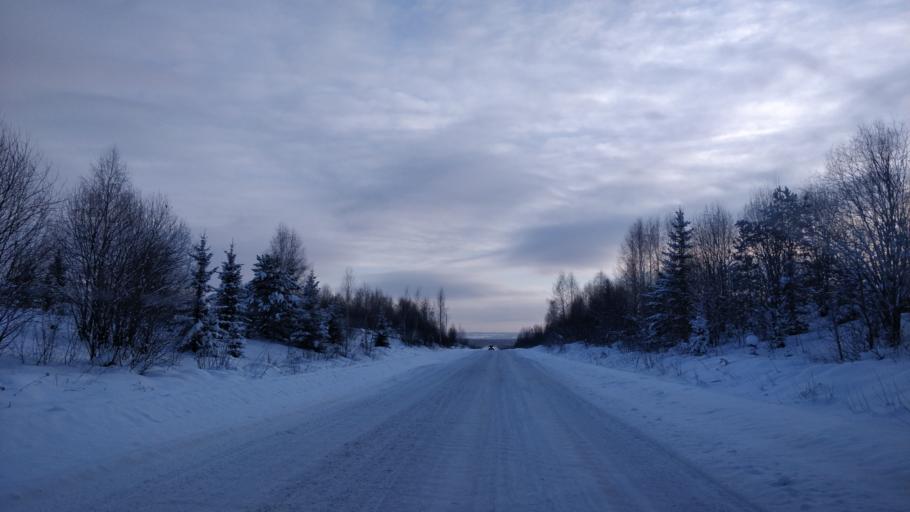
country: RU
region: Perm
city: Verkhnechusovskiye Gorodki
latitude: 58.2126
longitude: 57.1416
